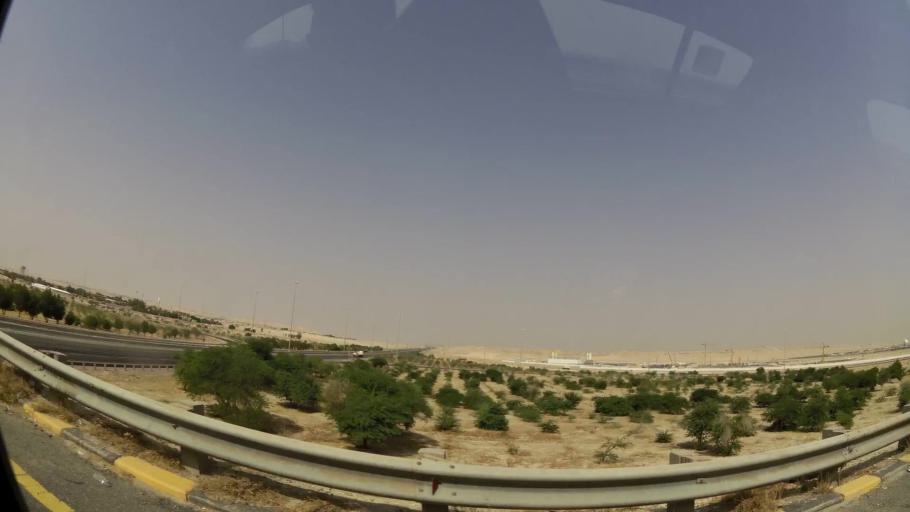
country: KW
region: Muhafazat al Jahra'
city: Al Jahra'
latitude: 29.3742
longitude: 47.6618
